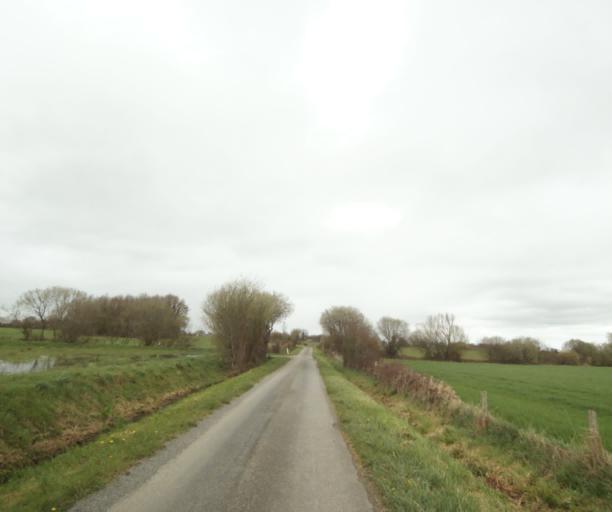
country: FR
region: Pays de la Loire
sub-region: Departement de la Loire-Atlantique
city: Bouvron
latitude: 47.4292
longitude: -1.8465
